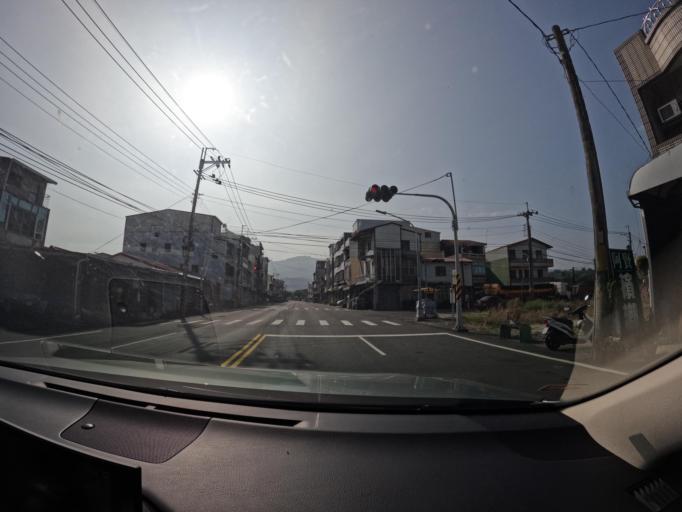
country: TW
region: Taiwan
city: Yujing
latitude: 23.0791
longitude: 120.4890
